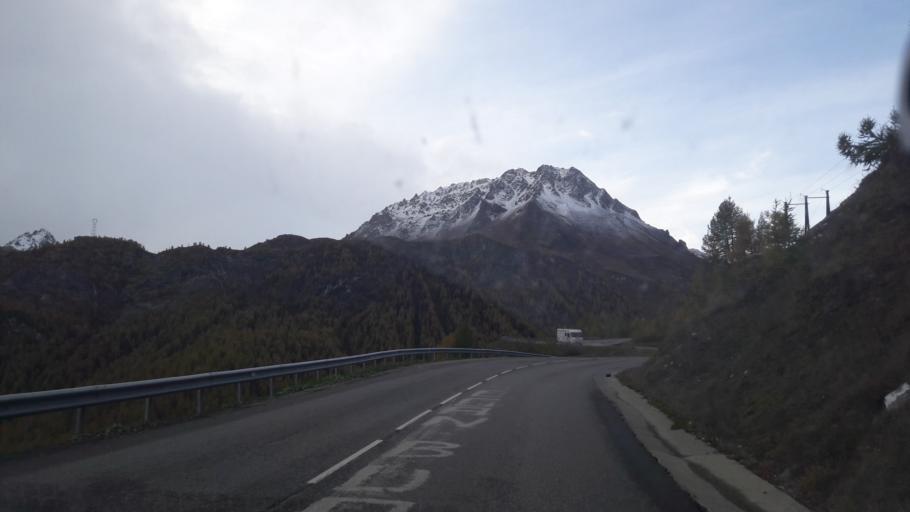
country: FR
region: Rhone-Alpes
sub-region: Departement de la Savoie
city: Tignes
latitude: 45.4839
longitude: 6.9269
